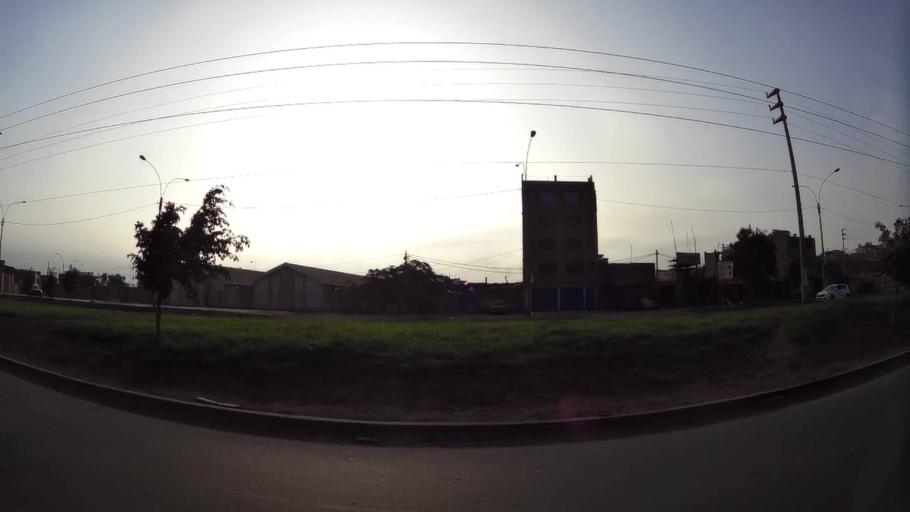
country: PE
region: Lima
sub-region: Lima
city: Independencia
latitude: -11.9717
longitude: -77.0856
